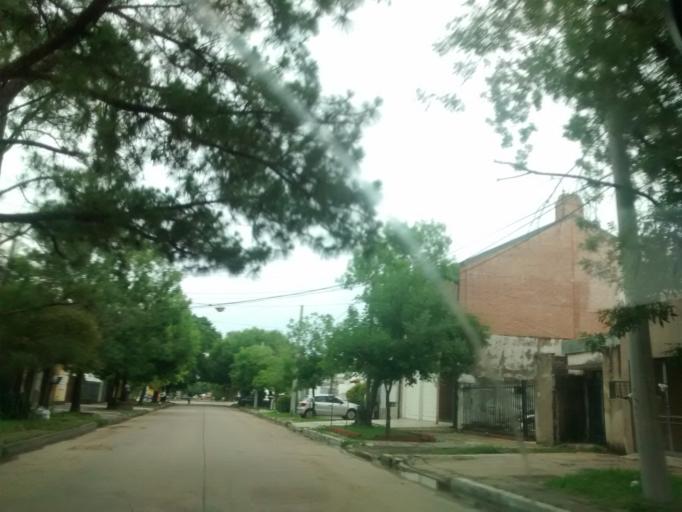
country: AR
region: Chaco
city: Resistencia
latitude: -27.4426
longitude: -58.9838
